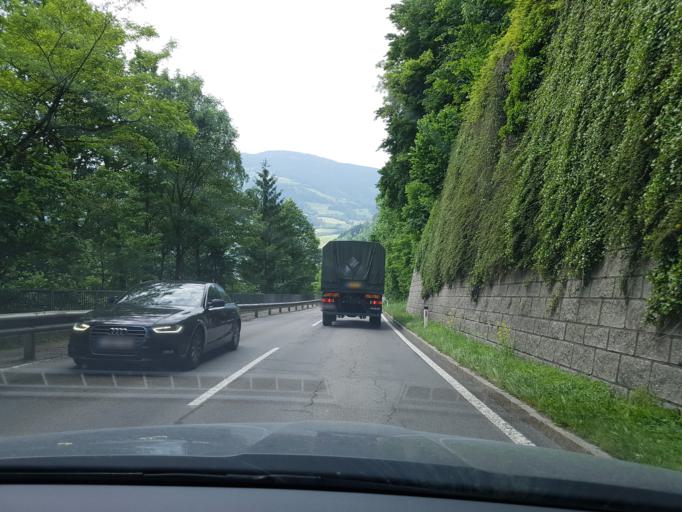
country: AT
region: Carinthia
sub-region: Politischer Bezirk Spittal an der Drau
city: Radenthein
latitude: 46.7982
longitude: 13.7230
